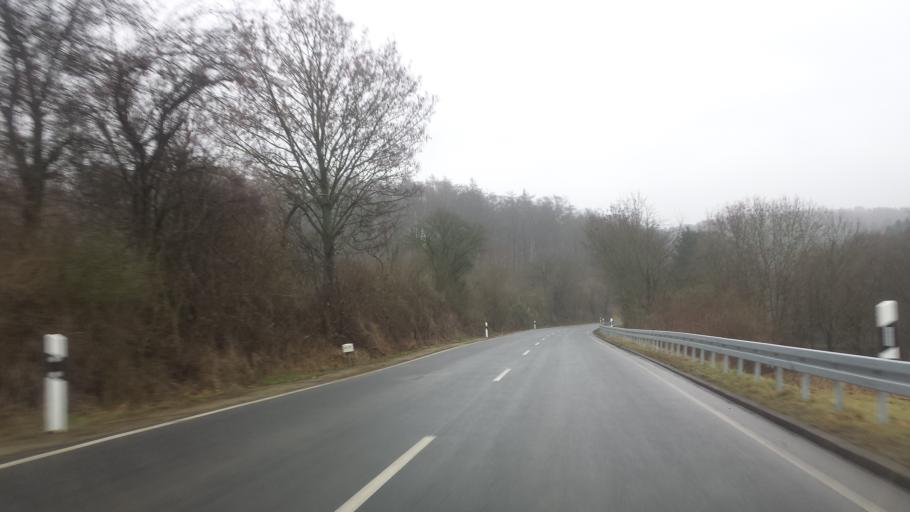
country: DE
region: Hesse
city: Ober-Ramstadt
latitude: 49.7849
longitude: 8.7118
